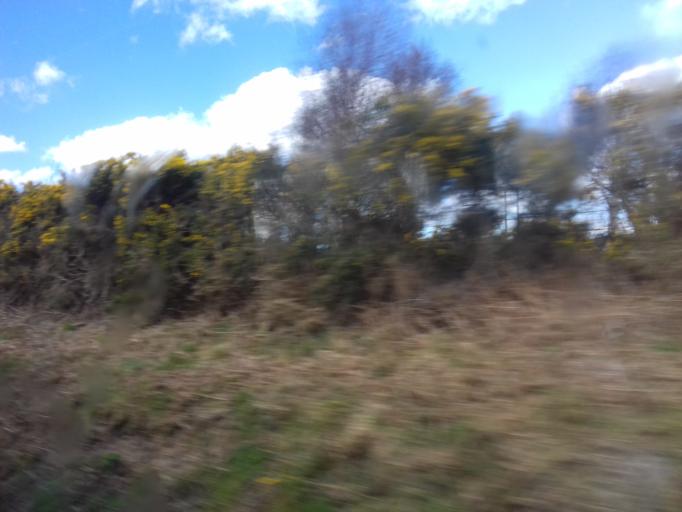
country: IE
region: Munster
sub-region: County Cork
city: Millstreet
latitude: 52.0789
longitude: -9.1820
